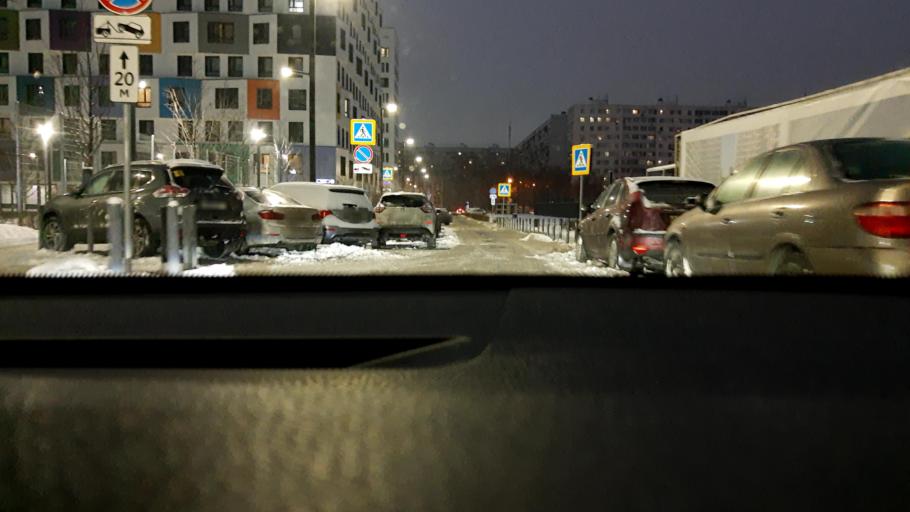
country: RU
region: Moscow
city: Sviblovo
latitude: 55.8506
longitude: 37.6203
